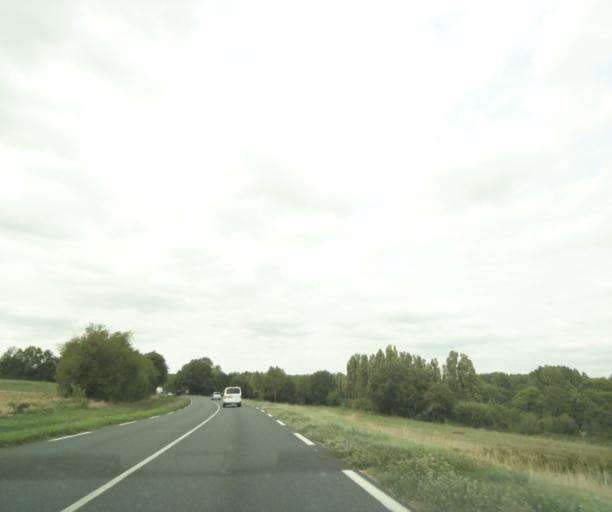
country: FR
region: Centre
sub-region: Departement de l'Indre
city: Chatillon-sur-Indre
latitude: 47.0446
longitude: 1.0953
